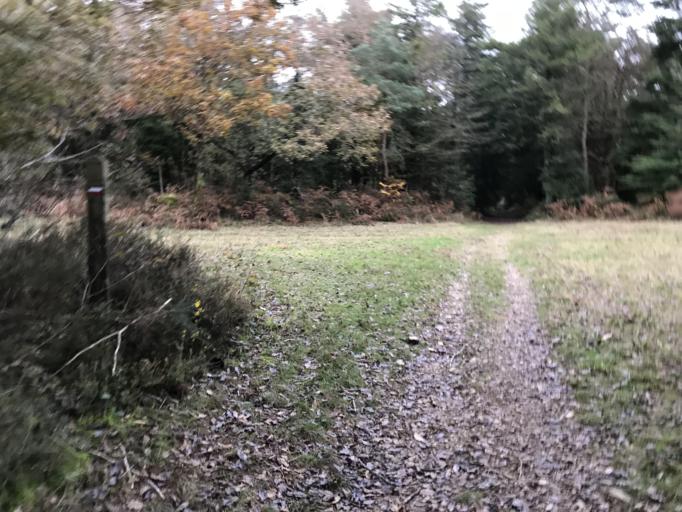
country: FR
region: Brittany
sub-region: Departement du Finistere
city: Hopital-Camfrout
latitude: 48.3352
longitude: -4.2132
